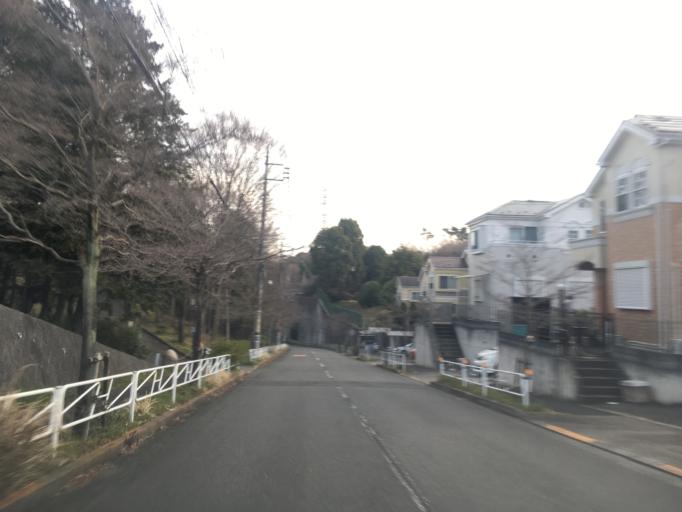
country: JP
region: Tokyo
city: Hino
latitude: 35.6247
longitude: 139.4071
